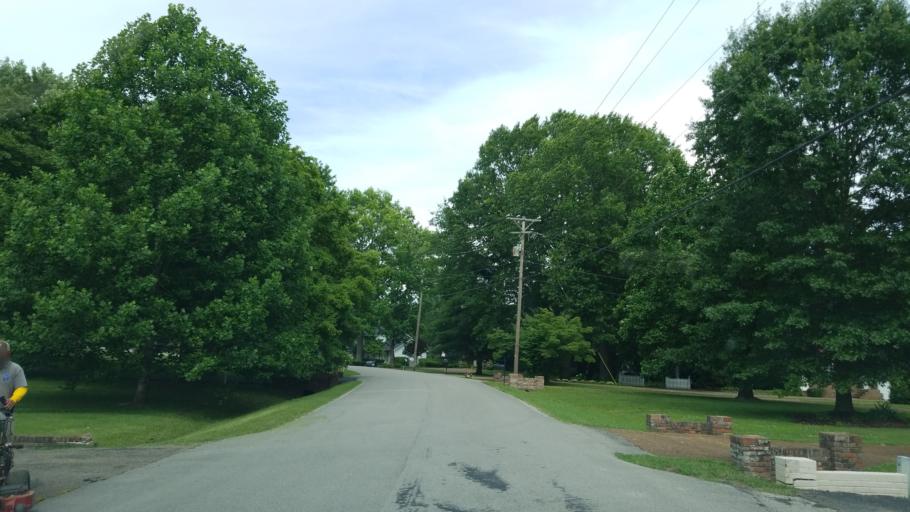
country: US
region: Tennessee
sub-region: Davidson County
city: Forest Hills
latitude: 36.0337
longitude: -86.8322
